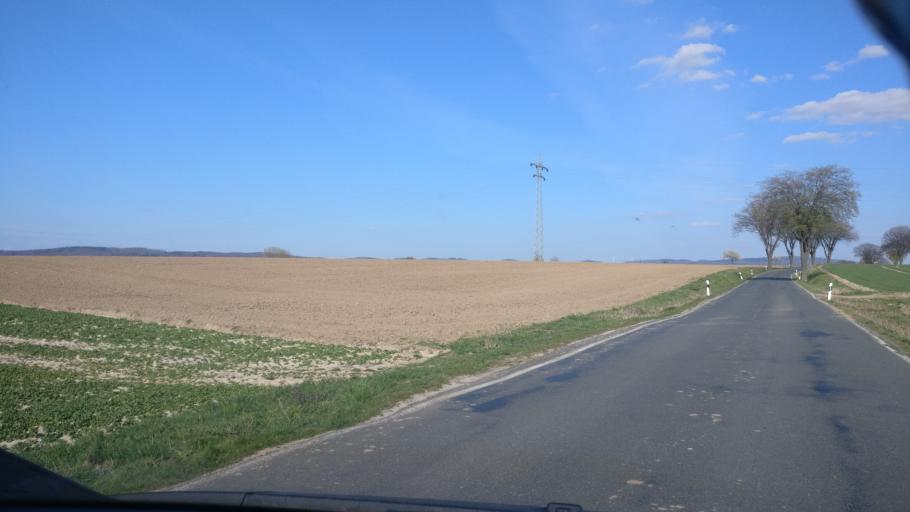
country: DE
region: North Rhine-Westphalia
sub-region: Regierungsbezirk Detmold
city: Lage
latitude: 52.0192
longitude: 8.8061
